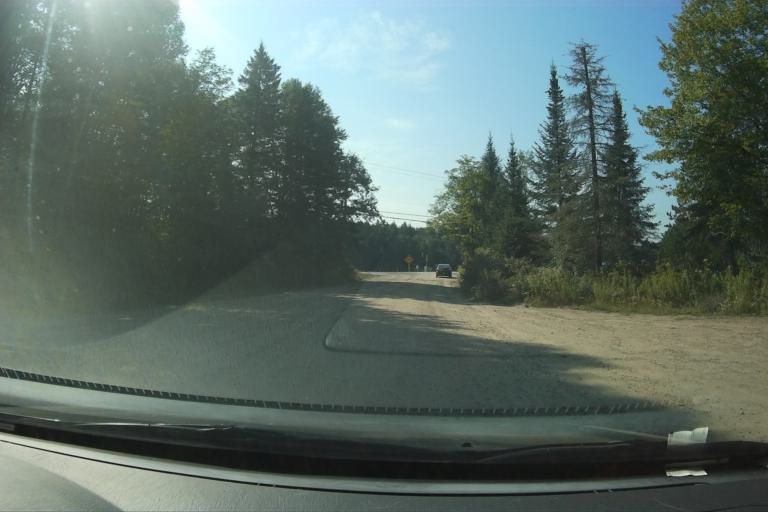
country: CA
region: Ontario
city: Huntsville
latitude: 45.5429
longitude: -78.6960
